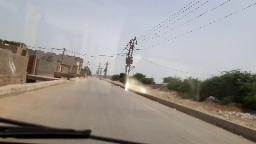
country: PK
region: Sindh
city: Malir Cantonment
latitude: 24.8357
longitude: 67.2054
